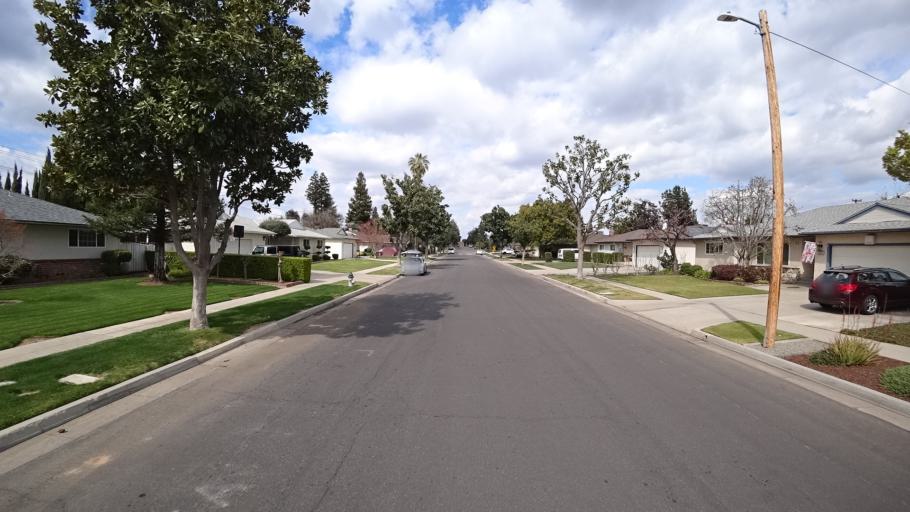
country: US
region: California
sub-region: Fresno County
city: Clovis
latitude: 36.8202
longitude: -119.7672
